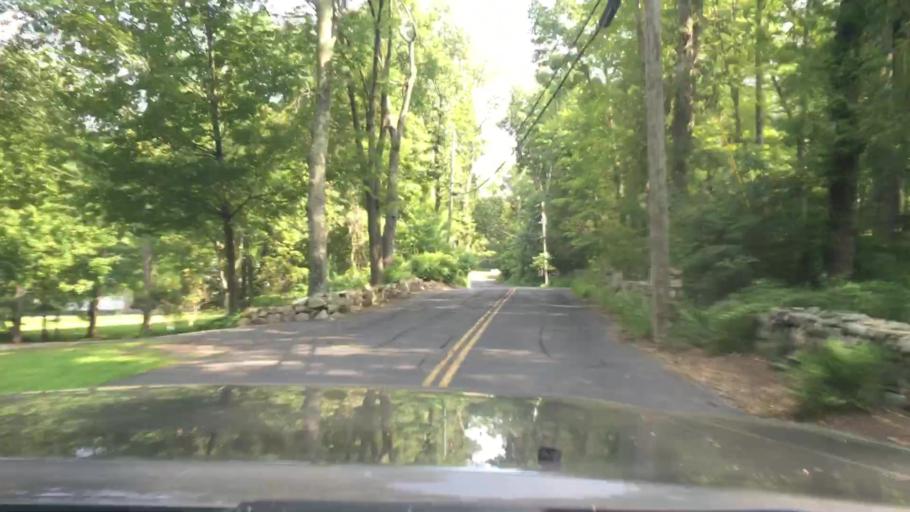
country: US
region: Connecticut
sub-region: Fairfield County
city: Georgetown
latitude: 41.2444
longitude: -73.4558
